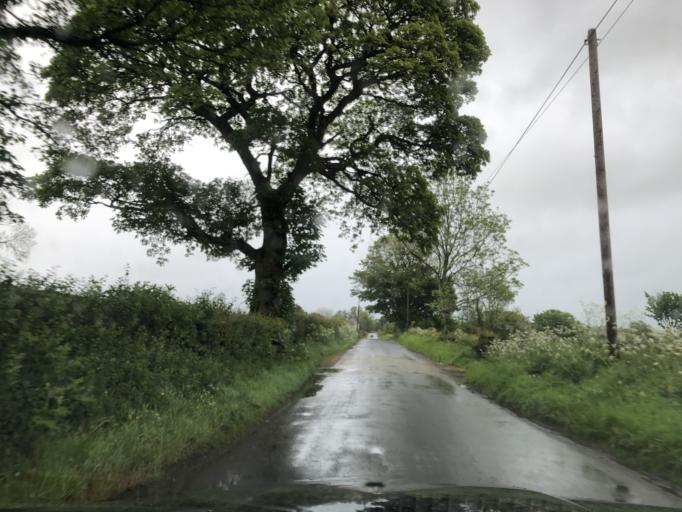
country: GB
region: Northern Ireland
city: Dunloy
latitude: 55.1326
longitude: -6.3721
